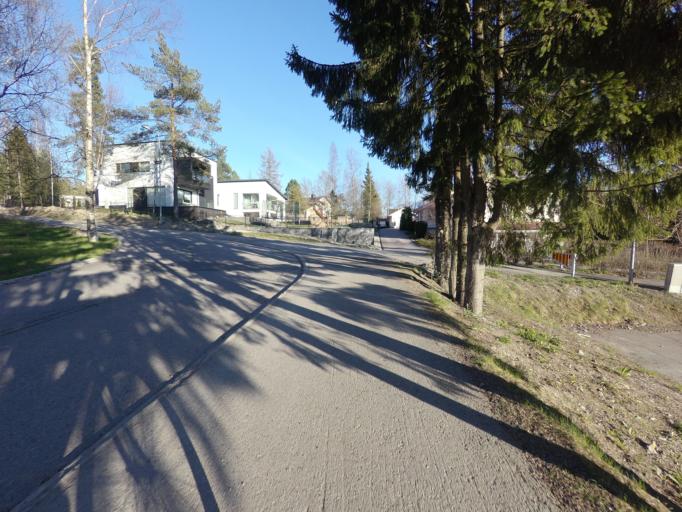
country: FI
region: Uusimaa
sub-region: Helsinki
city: Espoo
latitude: 60.1658
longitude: 24.6703
